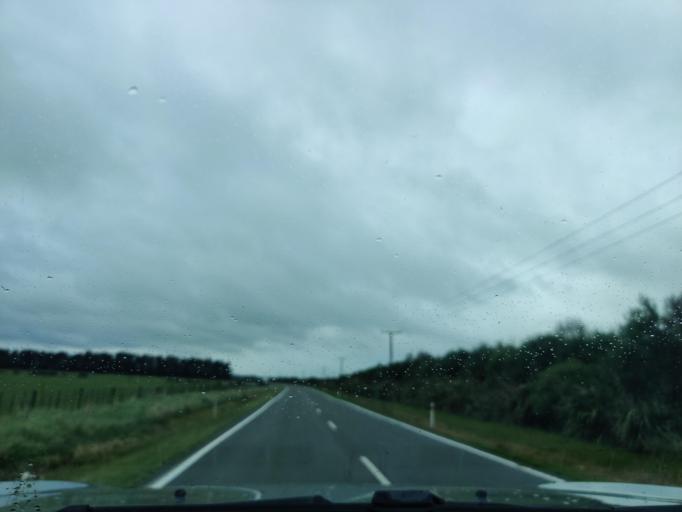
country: NZ
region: Hawke's Bay
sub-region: Hastings District
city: Hastings
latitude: -40.0075
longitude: 176.3847
